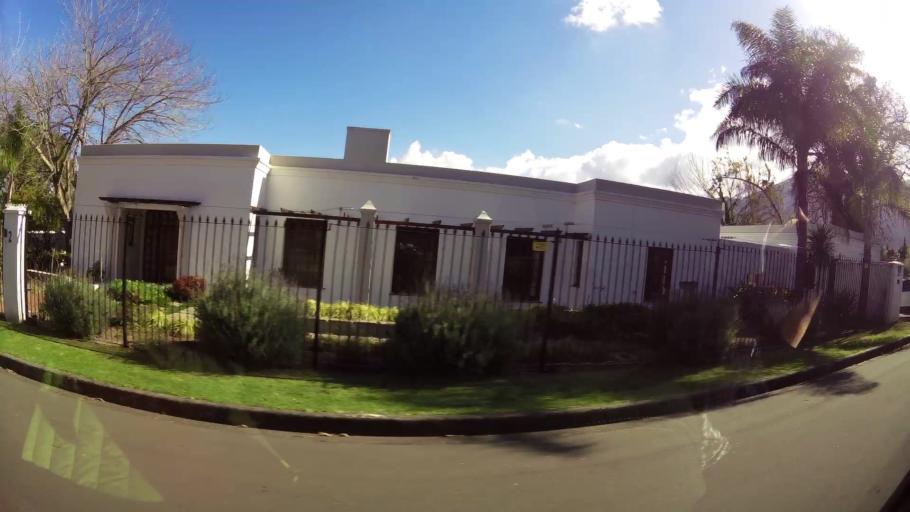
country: ZA
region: Western Cape
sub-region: Eden District Municipality
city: George
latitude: -33.9533
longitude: 22.4585
